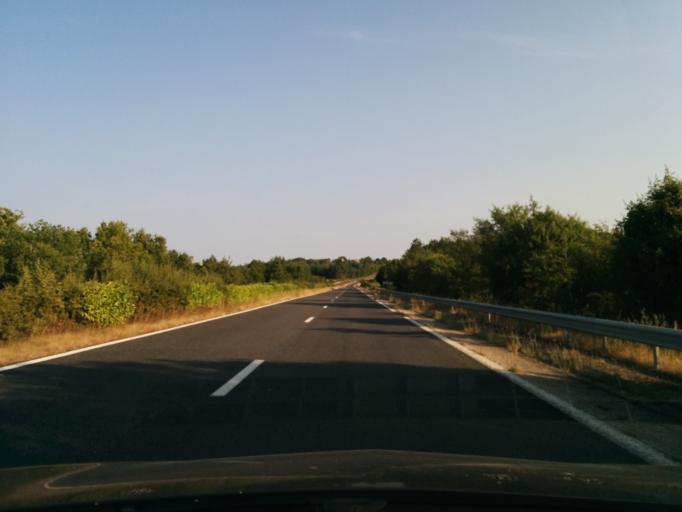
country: FR
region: Midi-Pyrenees
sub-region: Departement du Lot
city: Souillac
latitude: 44.8165
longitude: 1.4787
